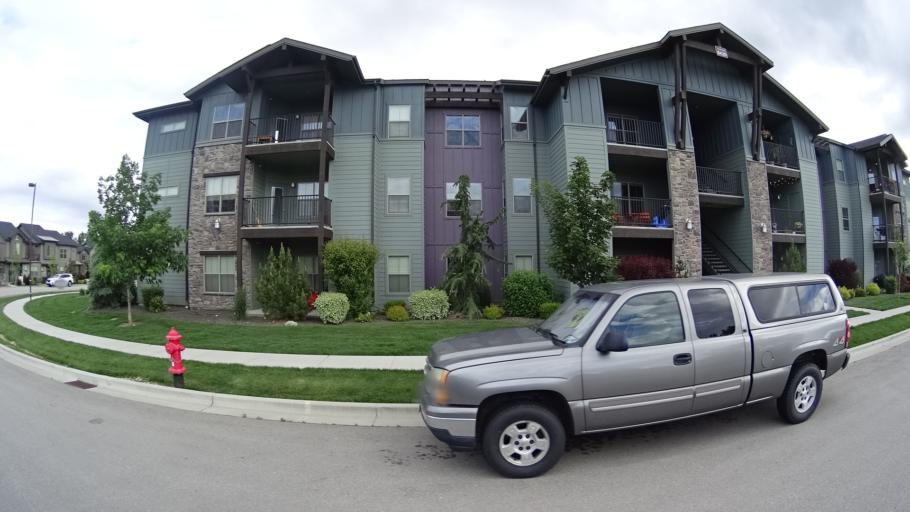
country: US
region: Idaho
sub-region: Ada County
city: Eagle
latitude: 43.6756
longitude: -116.2909
